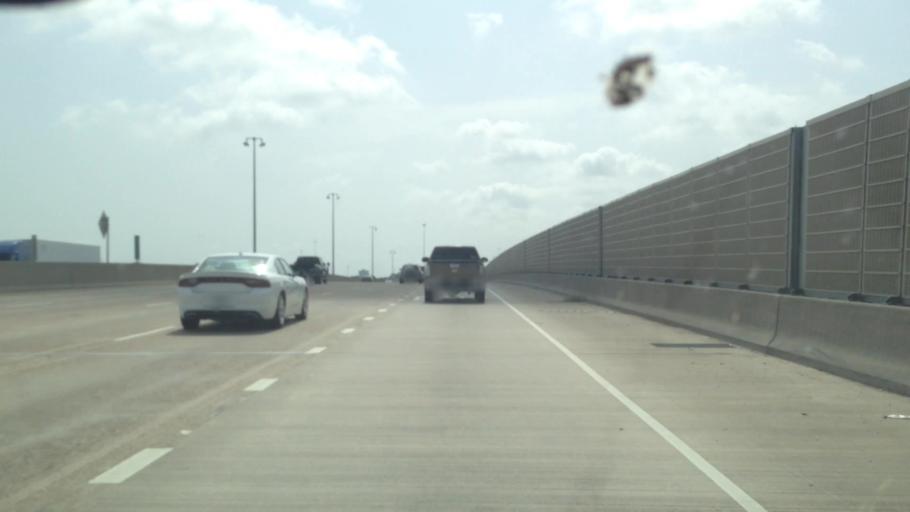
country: US
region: Louisiana
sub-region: Jefferson Parish
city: Metairie Terrace
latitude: 29.9994
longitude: -90.1940
